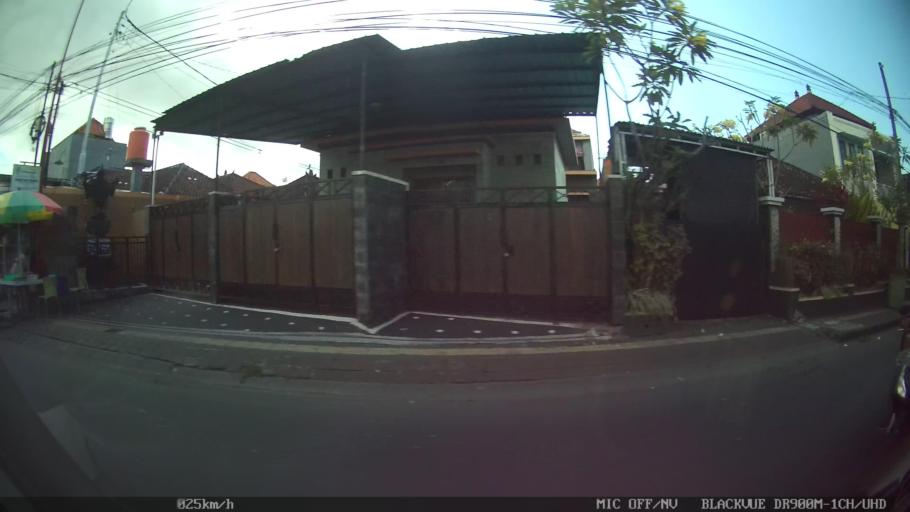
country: ID
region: Bali
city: Karyadharma
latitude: -8.6976
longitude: 115.1973
